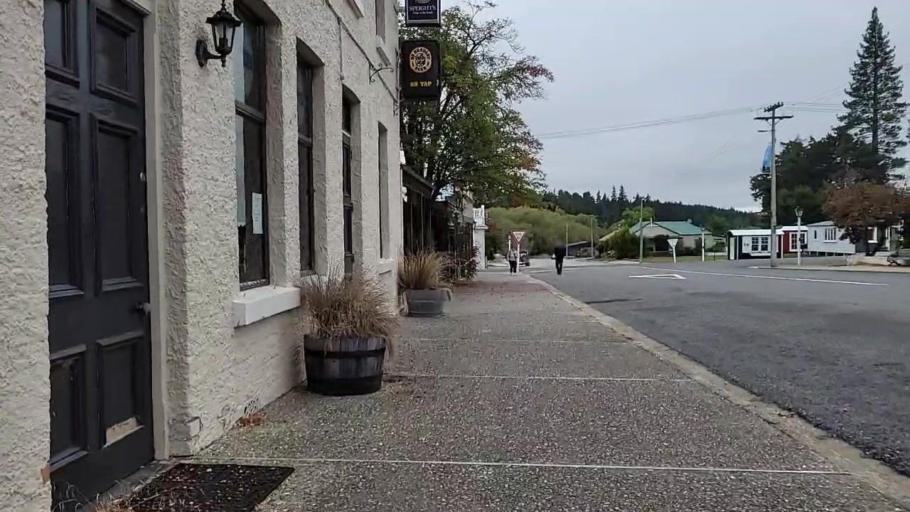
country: NZ
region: Otago
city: Oamaru
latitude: -45.0233
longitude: 170.1471
